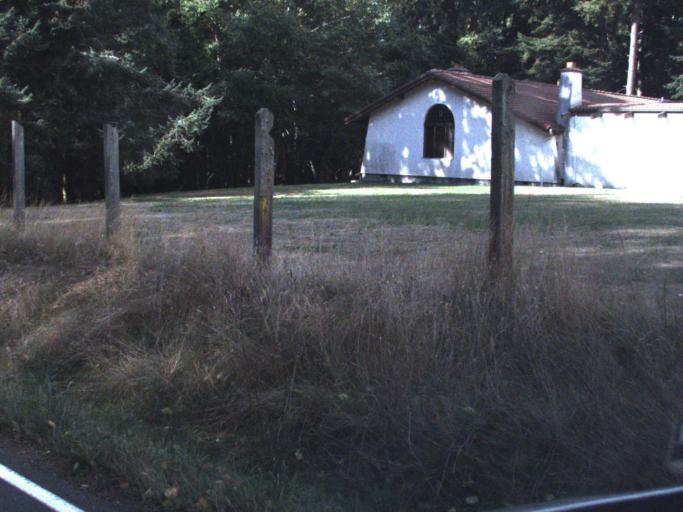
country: US
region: Washington
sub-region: Island County
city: Coupeville
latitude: 48.1709
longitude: -122.6185
